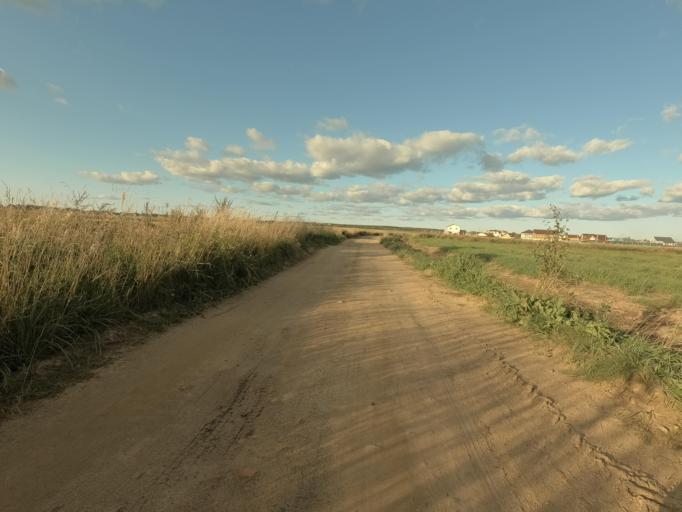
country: RU
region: Leningrad
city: Imeni Sverdlova
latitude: 59.8662
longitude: 30.7302
